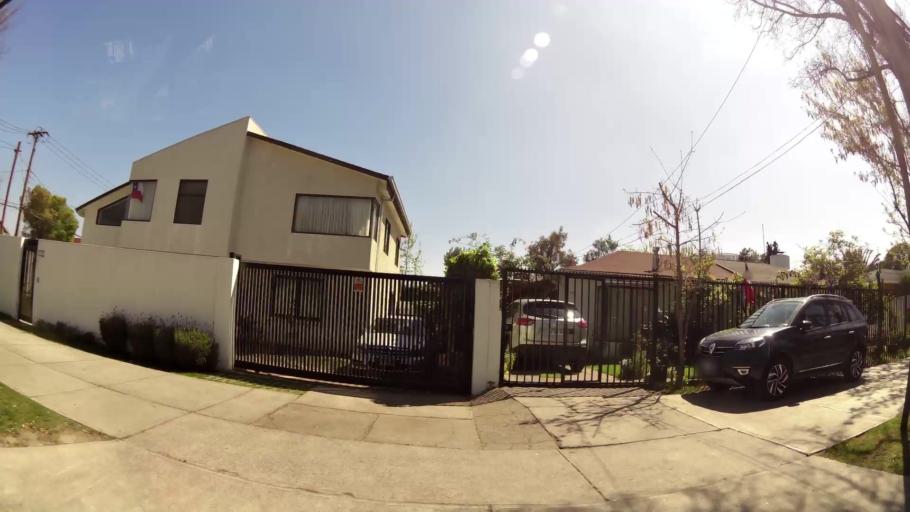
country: CL
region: Santiago Metropolitan
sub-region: Provincia de Santiago
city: Villa Presidente Frei, Nunoa, Santiago, Chile
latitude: -33.4112
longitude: -70.5576
